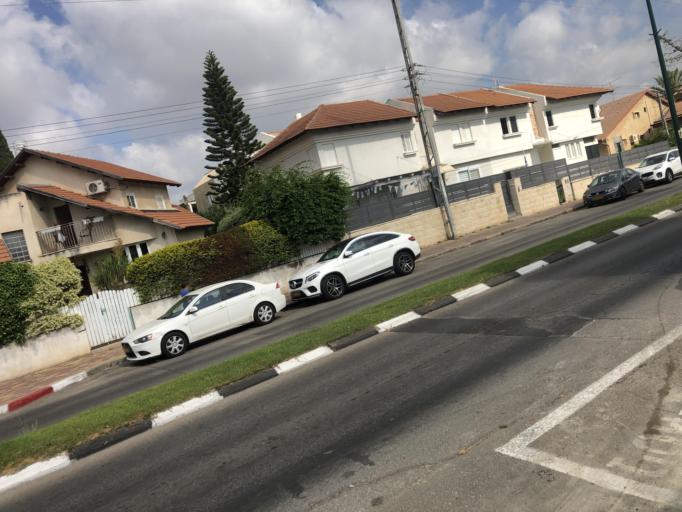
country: IL
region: Central District
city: Yehud
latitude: 32.0365
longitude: 34.8860
